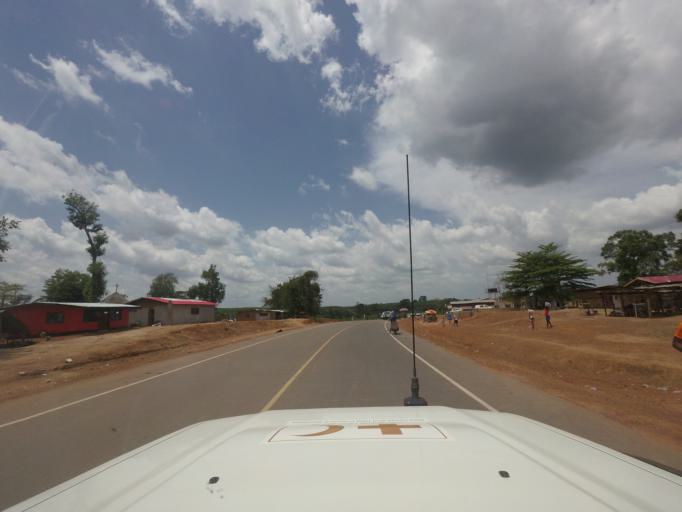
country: LR
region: Nimba
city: Sanniquellie
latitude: 7.2483
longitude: -8.9828
